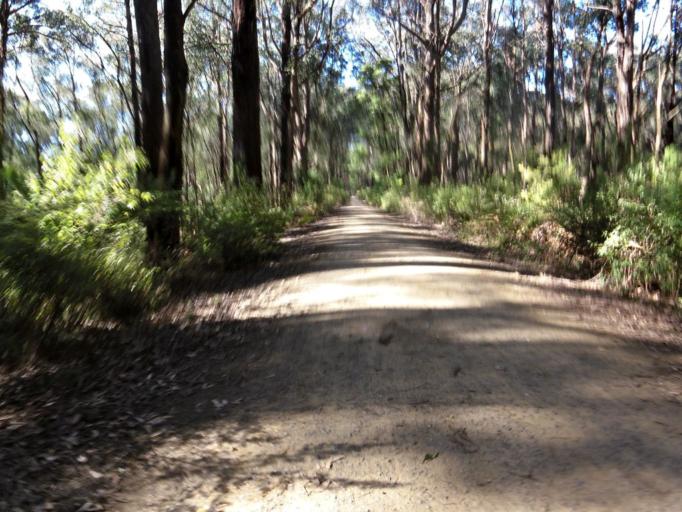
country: AU
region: Victoria
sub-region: Latrobe
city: Moe
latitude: -38.3972
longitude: 146.1757
